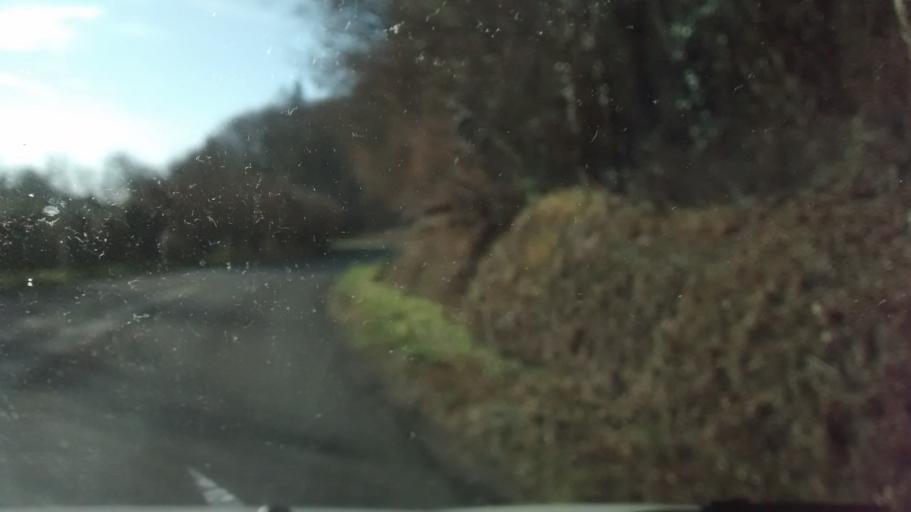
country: FR
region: Centre
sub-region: Departement d'Indre-et-Loire
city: Reugny
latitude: 47.4729
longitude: 0.8806
